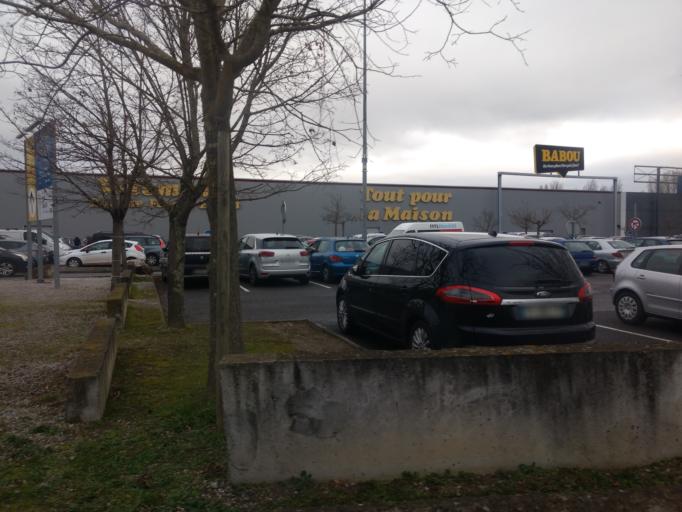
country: FR
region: Midi-Pyrenees
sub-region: Departement de la Haute-Garonne
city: Pinsaguel
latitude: 43.5155
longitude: 1.3744
